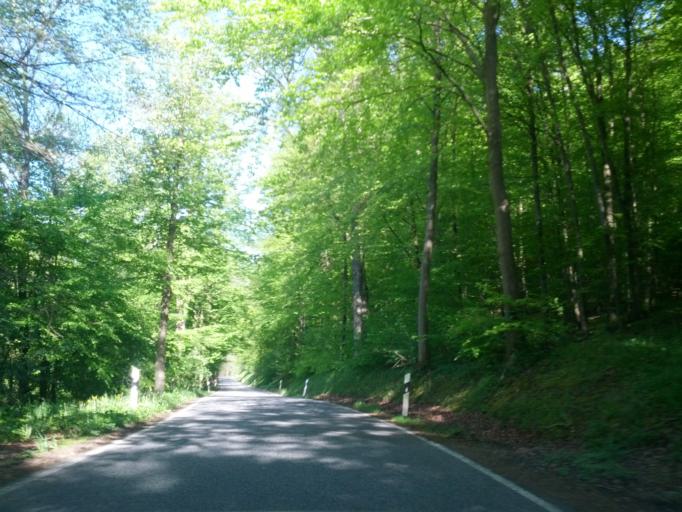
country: DE
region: Thuringia
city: Mackenrode
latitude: 51.3065
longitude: 10.0455
